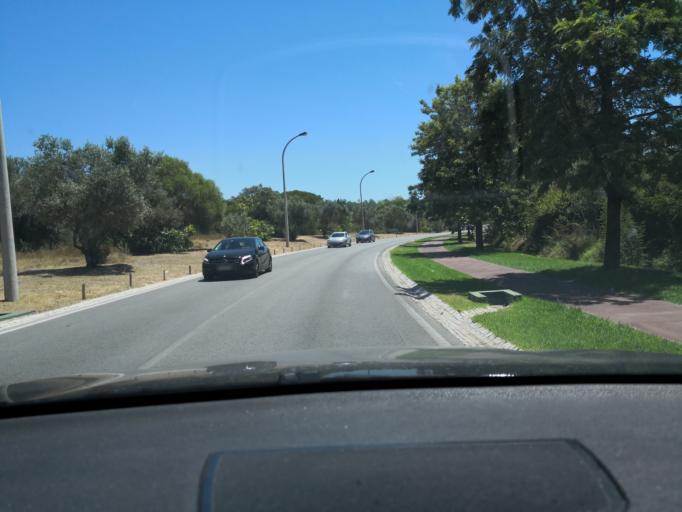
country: PT
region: Faro
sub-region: Loule
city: Vilamoura
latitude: 37.1038
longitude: -8.1265
